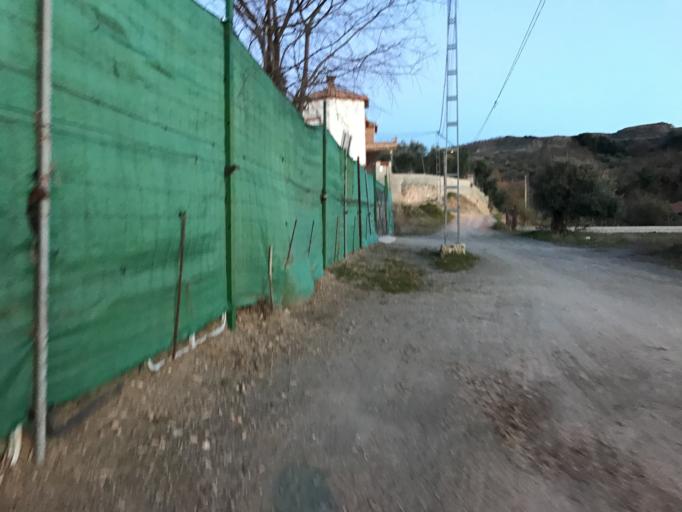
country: ES
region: Andalusia
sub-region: Provincia de Granada
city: Beas de Granada
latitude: 37.2212
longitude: -3.4788
